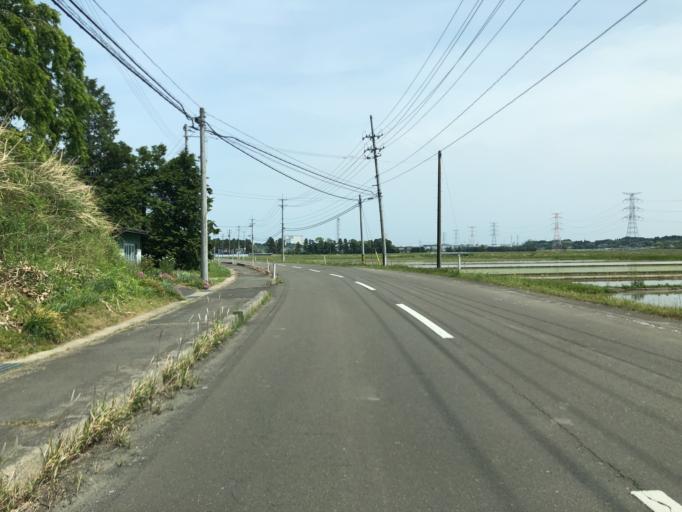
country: JP
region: Miyagi
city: Marumori
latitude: 37.8485
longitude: 140.9066
